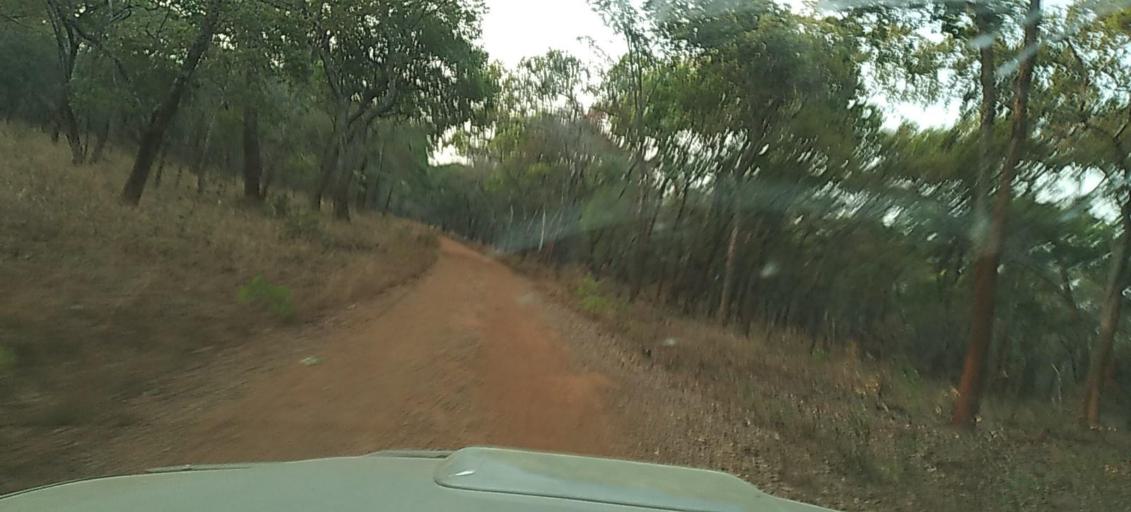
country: ZM
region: North-Western
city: Kasempa
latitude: -13.1047
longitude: 26.4052
